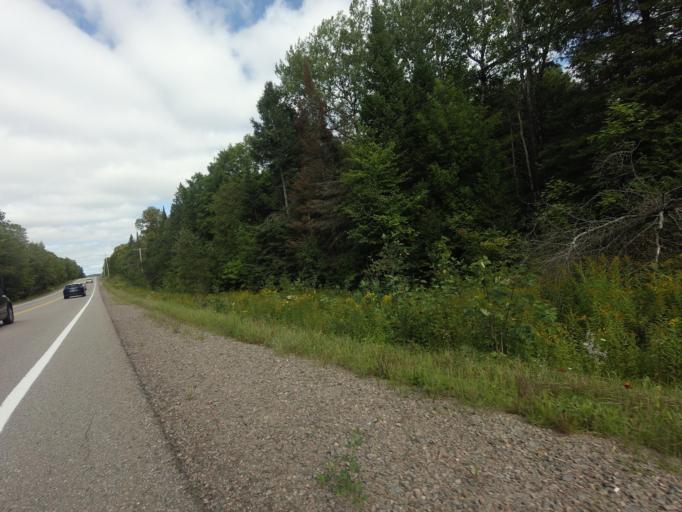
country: CA
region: Ontario
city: Bancroft
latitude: 44.9521
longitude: -78.2916
